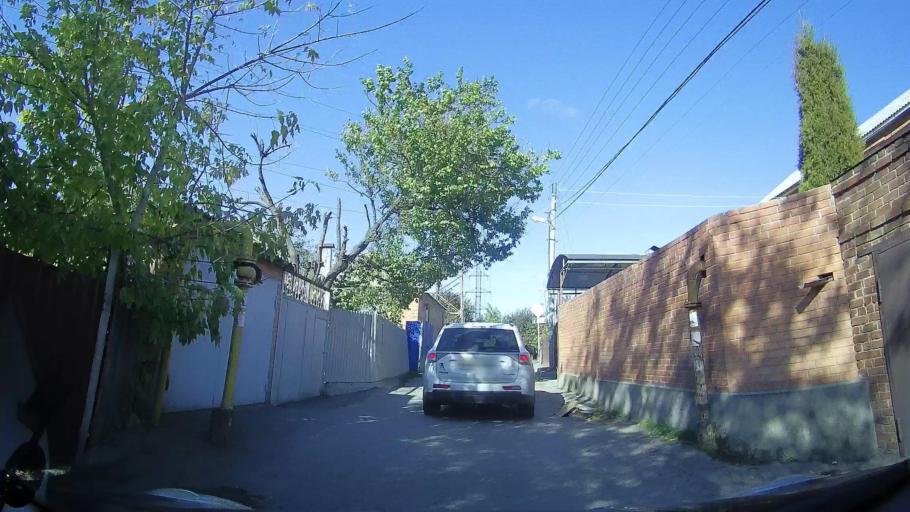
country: RU
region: Rostov
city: Rostov-na-Donu
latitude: 47.2385
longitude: 39.6728
